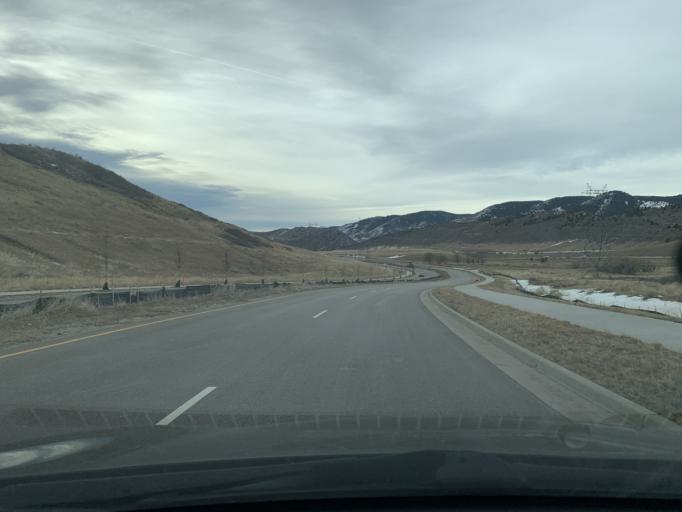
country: US
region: Colorado
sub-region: Jefferson County
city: West Pleasant View
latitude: 39.6817
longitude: -105.1830
